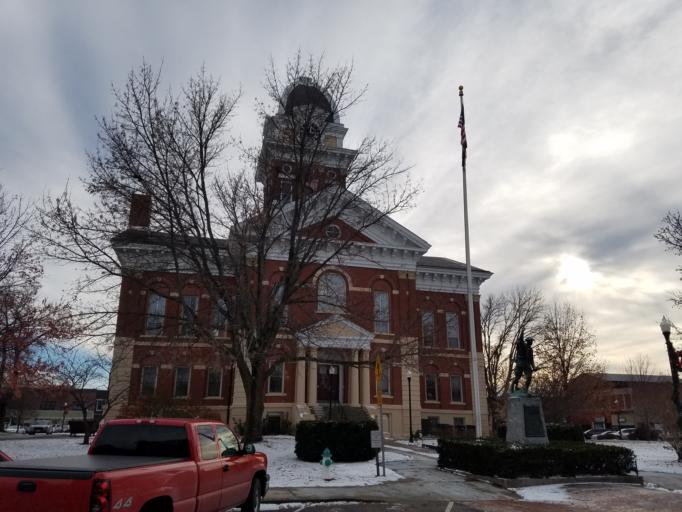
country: US
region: Missouri
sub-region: Saline County
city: Marshall
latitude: 39.1214
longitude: -93.1963
